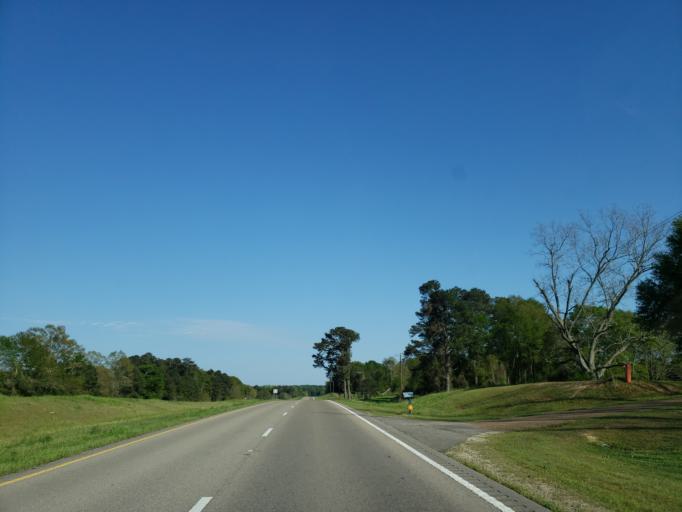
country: US
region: Mississippi
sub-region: Jones County
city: Ellisville
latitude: 31.6872
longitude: -89.3239
